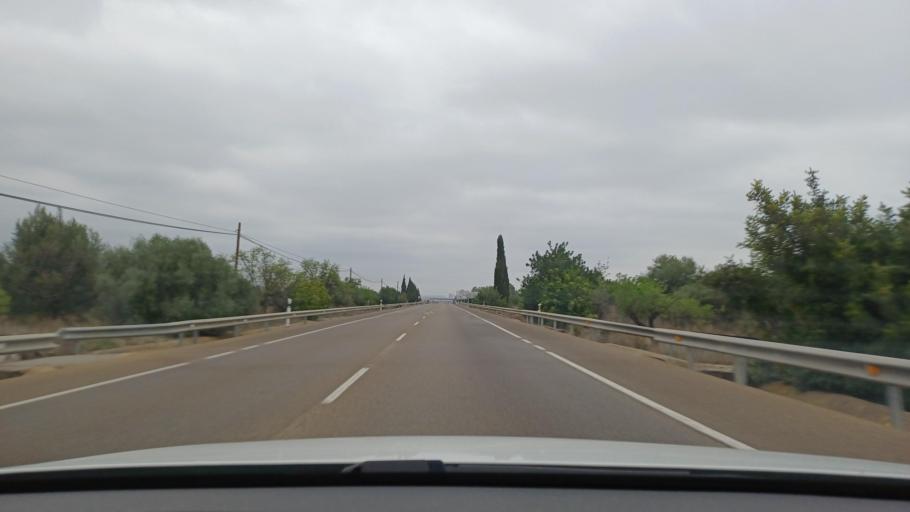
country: ES
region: Valencia
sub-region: Provincia de Castello
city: Orpesa/Oropesa del Mar
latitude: 40.1123
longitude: 0.1393
